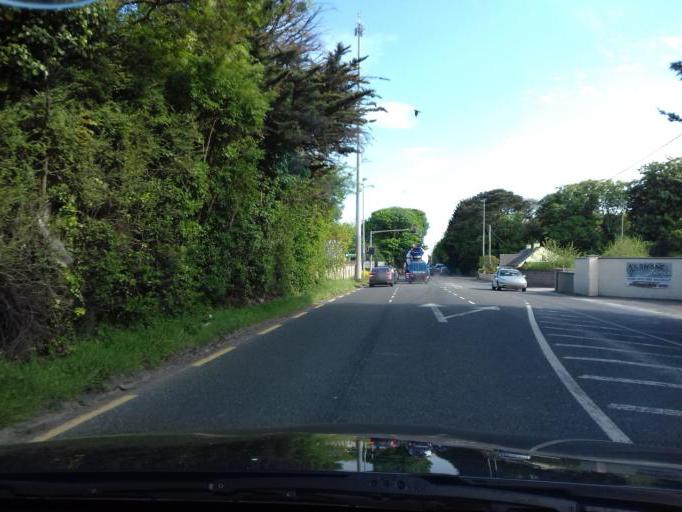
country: IE
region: Leinster
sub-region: Dublin City
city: Finglas
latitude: 53.4242
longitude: -6.3268
